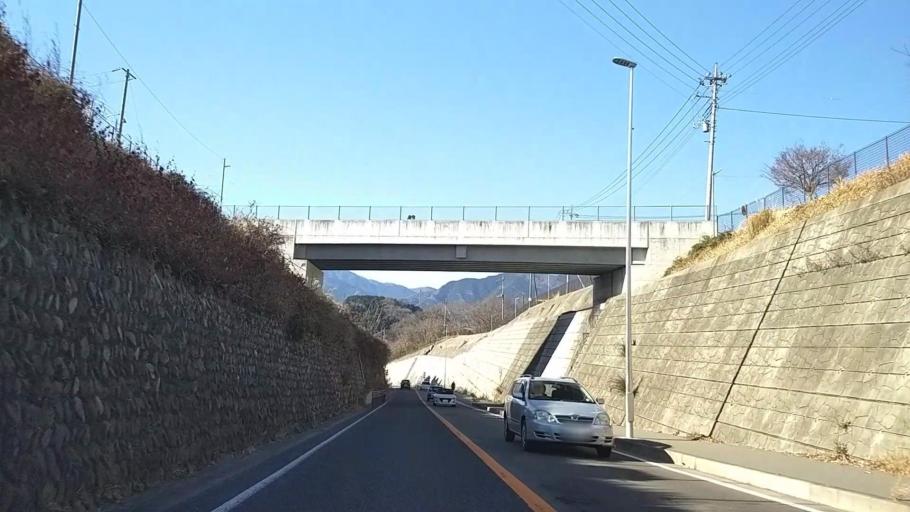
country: JP
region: Yamanashi
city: Uenohara
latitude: 35.6295
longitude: 139.1078
